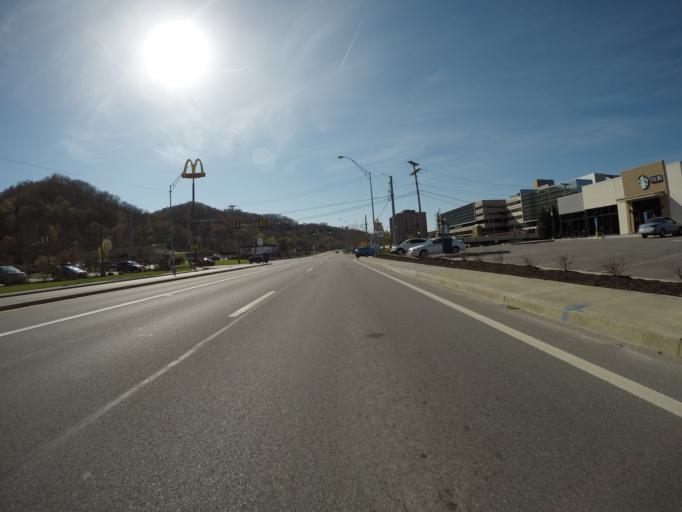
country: US
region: West Virginia
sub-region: Kanawha County
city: Charleston
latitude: 38.3285
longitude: -81.6004
